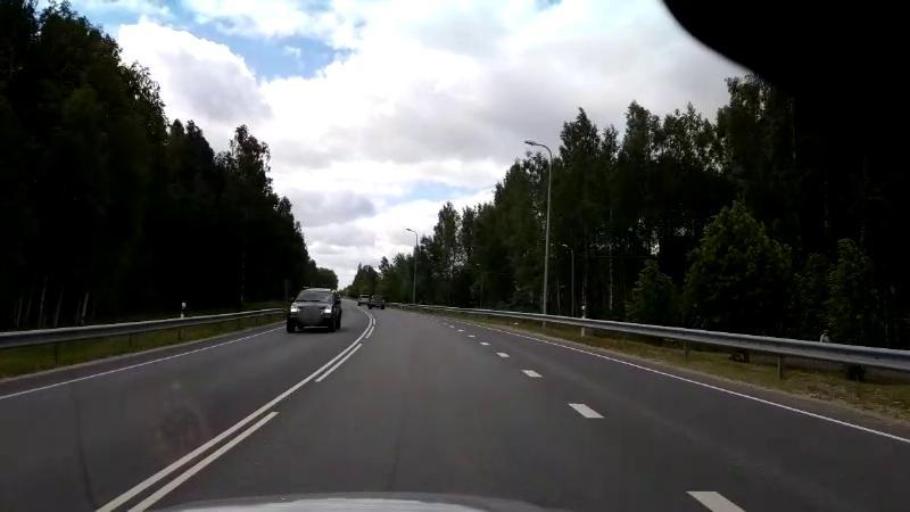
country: EE
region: Paernumaa
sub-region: Sauga vald
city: Sauga
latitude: 58.4222
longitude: 24.4946
